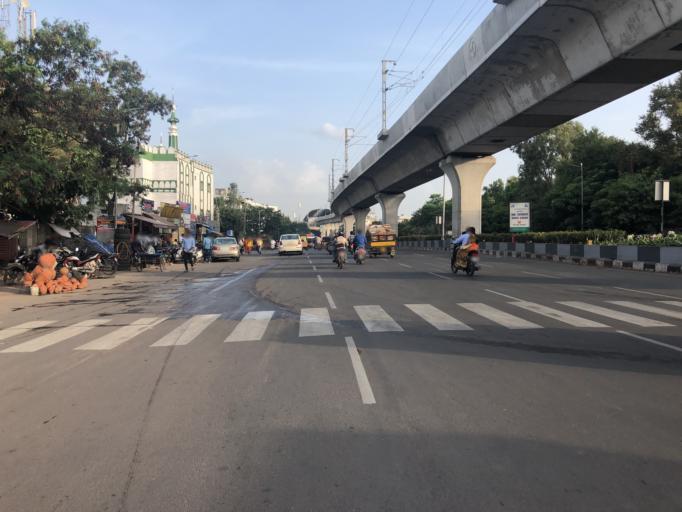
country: IN
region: Telangana
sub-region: Rangareddi
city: Kukatpalli
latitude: 17.4511
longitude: 78.4366
